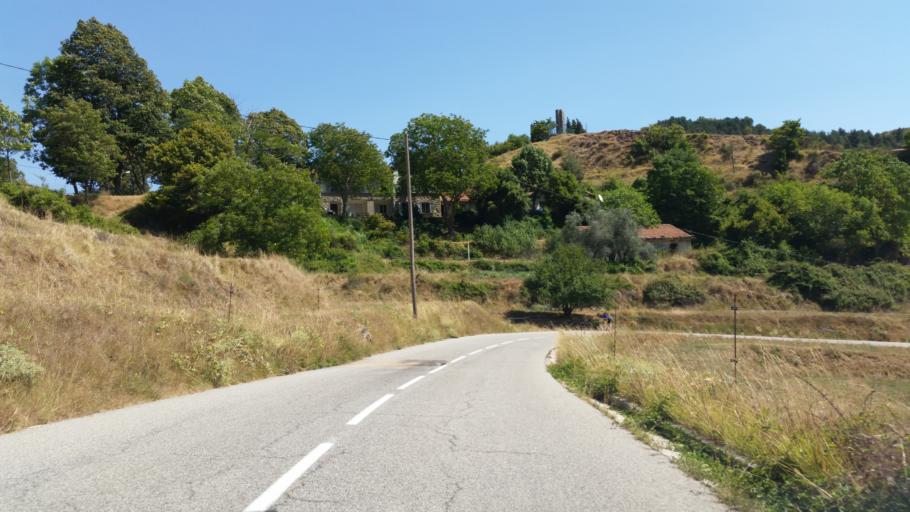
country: FR
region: Provence-Alpes-Cote d'Azur
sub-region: Departement des Alpes-Maritimes
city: Breil-sur-Roya
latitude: 43.9235
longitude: 7.4756
